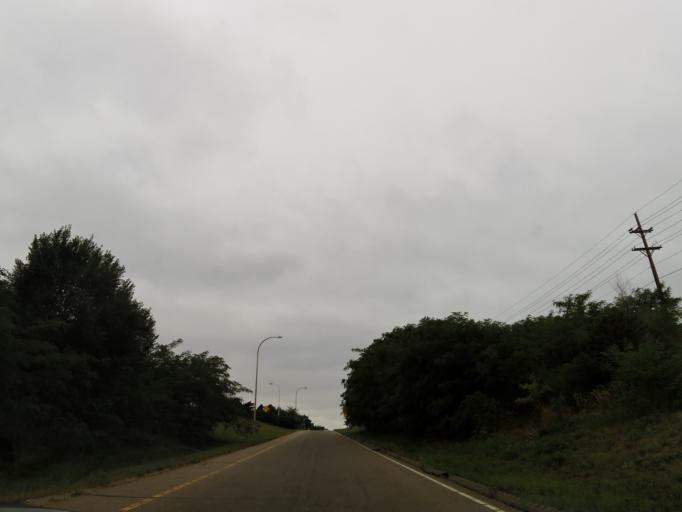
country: US
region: Colorado
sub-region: El Paso County
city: Colorado Springs
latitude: 38.7960
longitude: -104.8228
